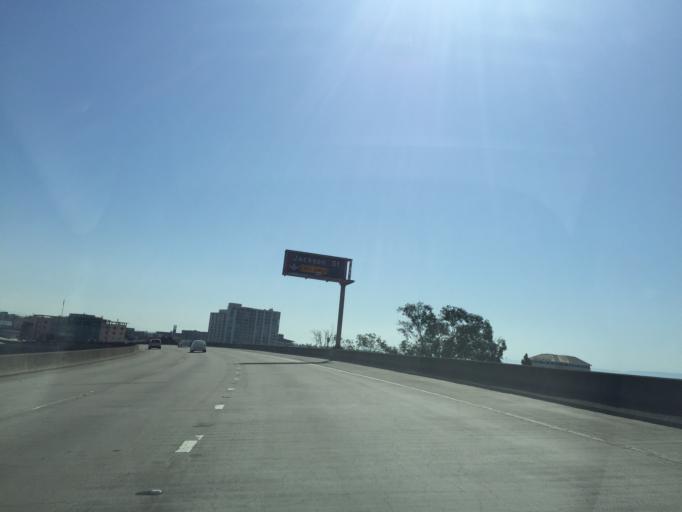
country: US
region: California
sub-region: Alameda County
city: Oakland
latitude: 37.8008
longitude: -122.2798
